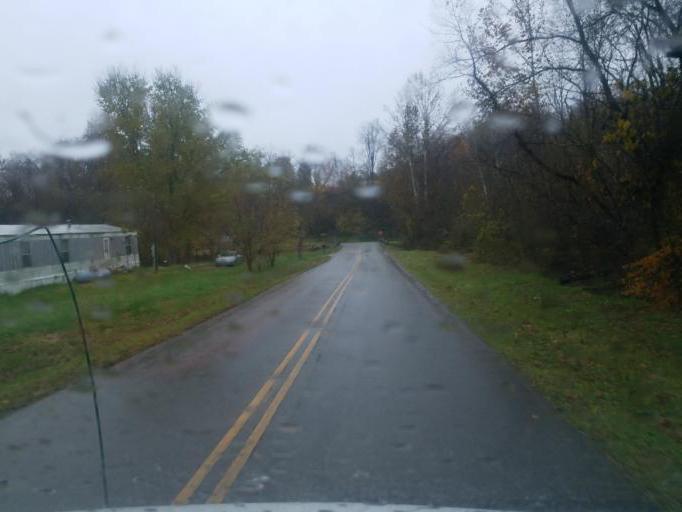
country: US
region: Ohio
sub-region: Washington County
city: Beverly
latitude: 39.4642
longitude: -81.6283
